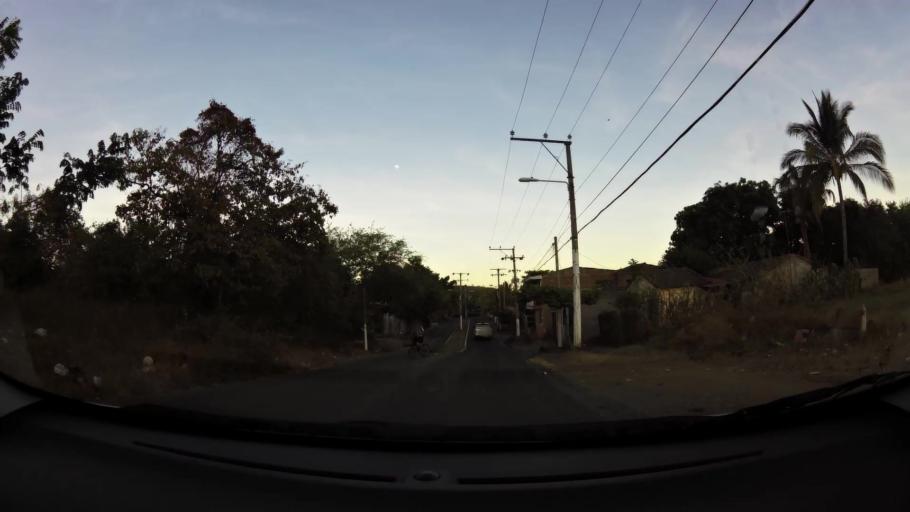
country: SV
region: San Miguel
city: San Miguel
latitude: 13.4786
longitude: -88.1608
